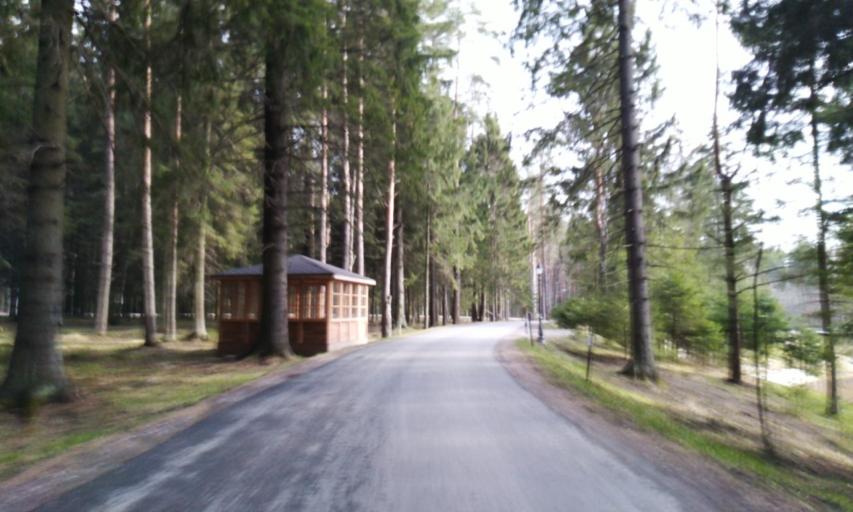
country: RU
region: Leningrad
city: Toksovo
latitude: 60.1291
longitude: 30.4529
